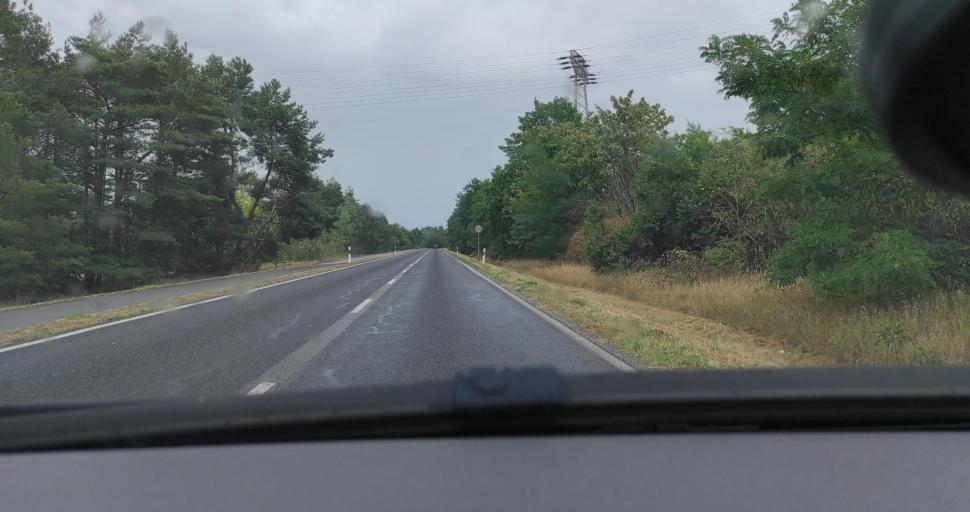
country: DE
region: Brandenburg
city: Cottbus
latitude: 51.7731
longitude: 14.3859
